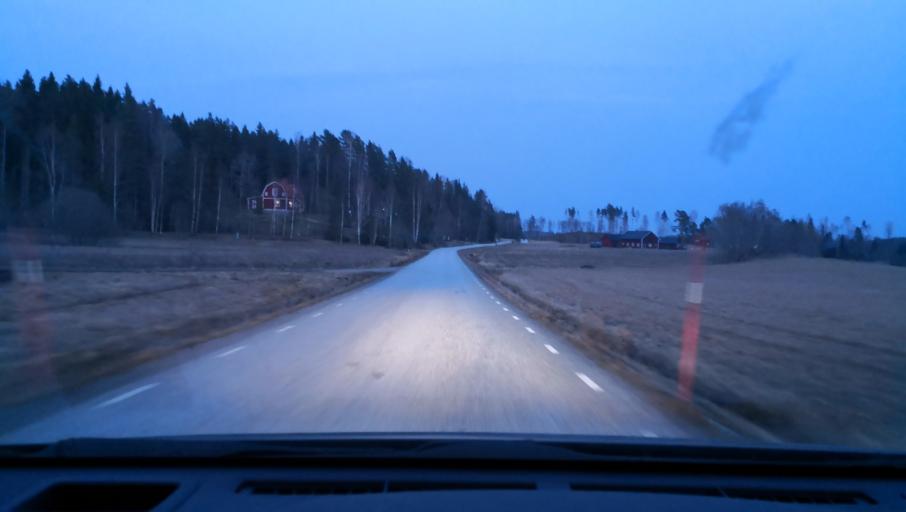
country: SE
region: OErebro
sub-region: Lindesbergs Kommun
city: Frovi
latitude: 59.5828
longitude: 15.4581
